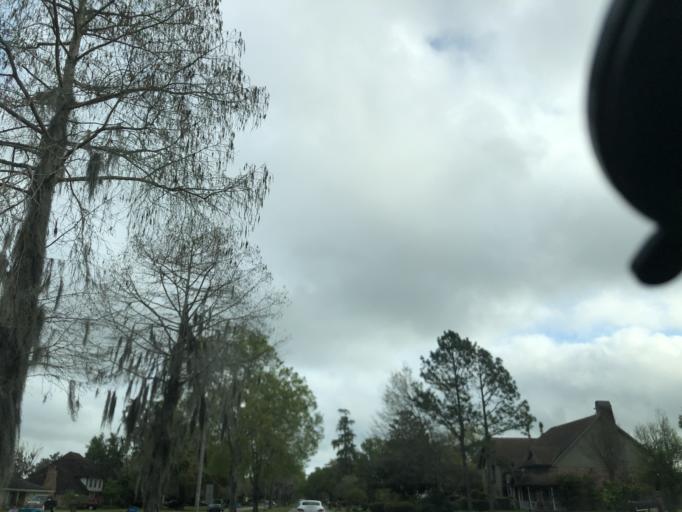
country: US
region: Louisiana
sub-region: Saint Charles Parish
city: New Sarpy
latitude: 29.9718
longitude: -90.3661
